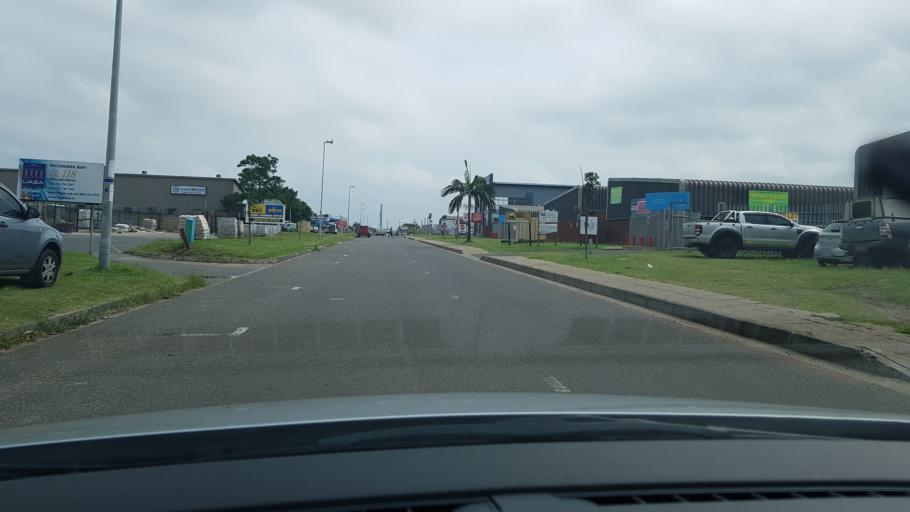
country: ZA
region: KwaZulu-Natal
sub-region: uThungulu District Municipality
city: Richards Bay
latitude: -28.7536
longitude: 32.0445
